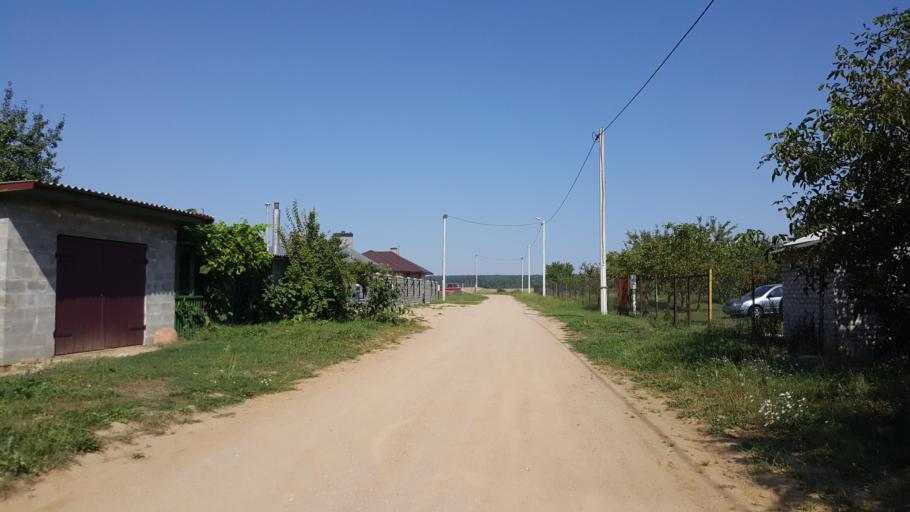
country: BY
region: Brest
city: Vysokaye
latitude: 52.4133
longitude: 23.4672
